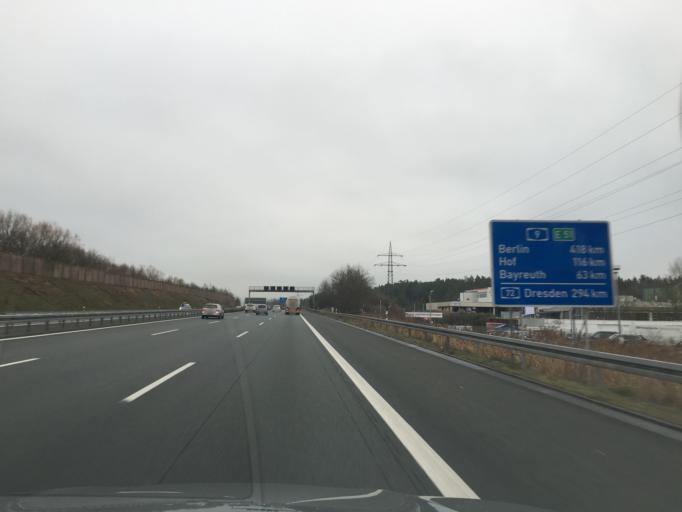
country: DE
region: Bavaria
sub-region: Regierungsbezirk Mittelfranken
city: Lauf an der Pegnitz
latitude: 49.5031
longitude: 11.2898
